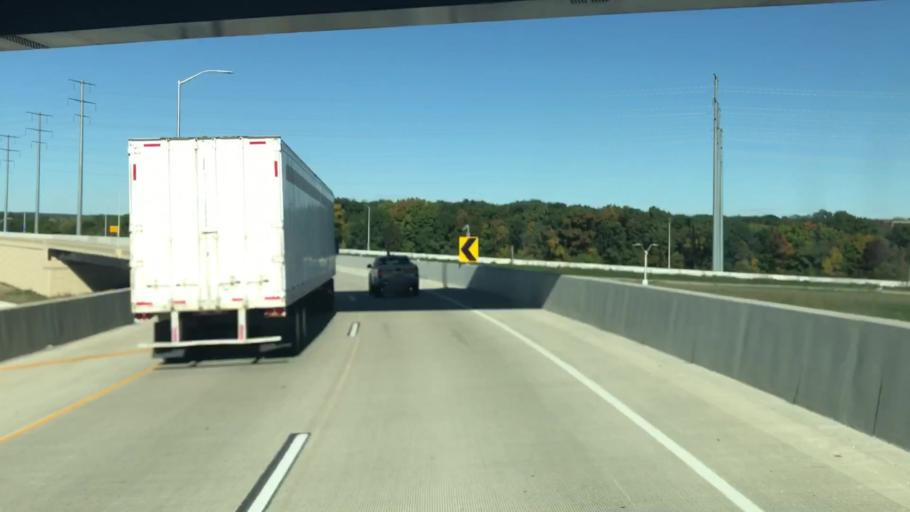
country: US
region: Wisconsin
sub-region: Milwaukee County
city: West Allis
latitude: 43.0266
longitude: -88.0365
